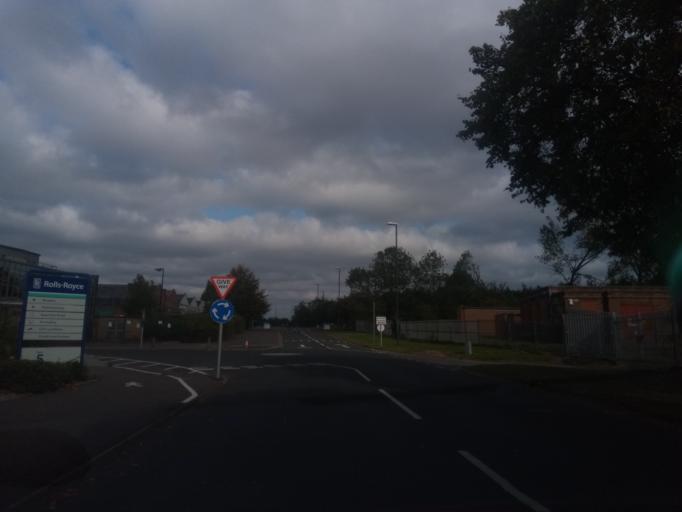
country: GB
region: England
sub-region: Derby
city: Derby
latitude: 52.8853
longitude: -1.4623
